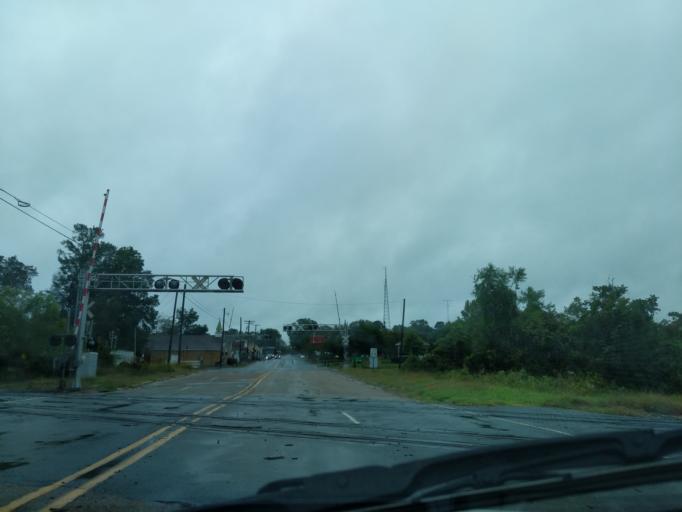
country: US
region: Louisiana
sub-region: Bienville Parish
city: Arcadia
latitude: 32.5473
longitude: -93.0530
